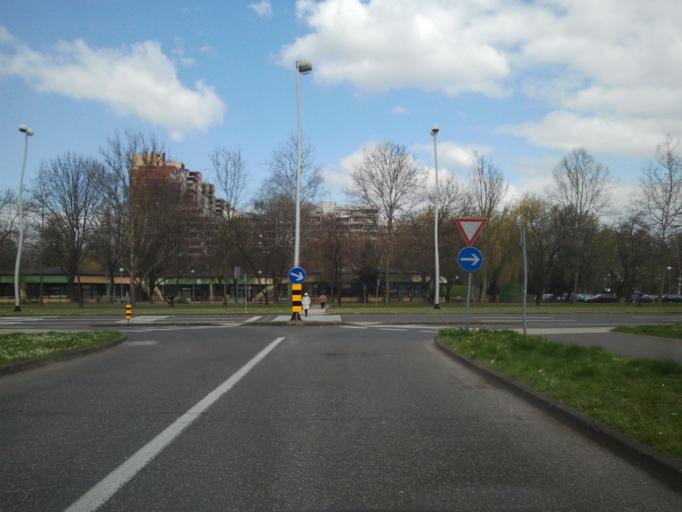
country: HR
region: Grad Zagreb
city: Novi Zagreb
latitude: 45.7675
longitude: 15.9957
